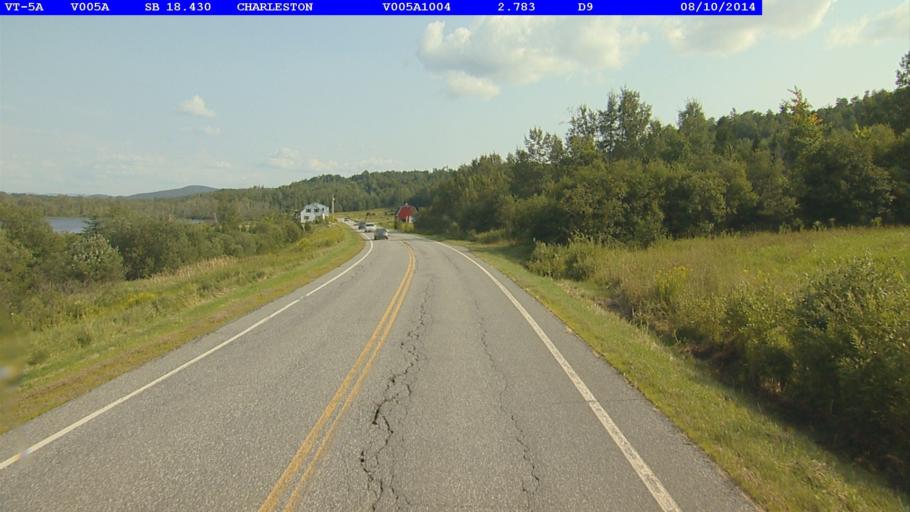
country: US
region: Vermont
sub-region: Orleans County
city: Newport
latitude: 44.8705
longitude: -72.0605
